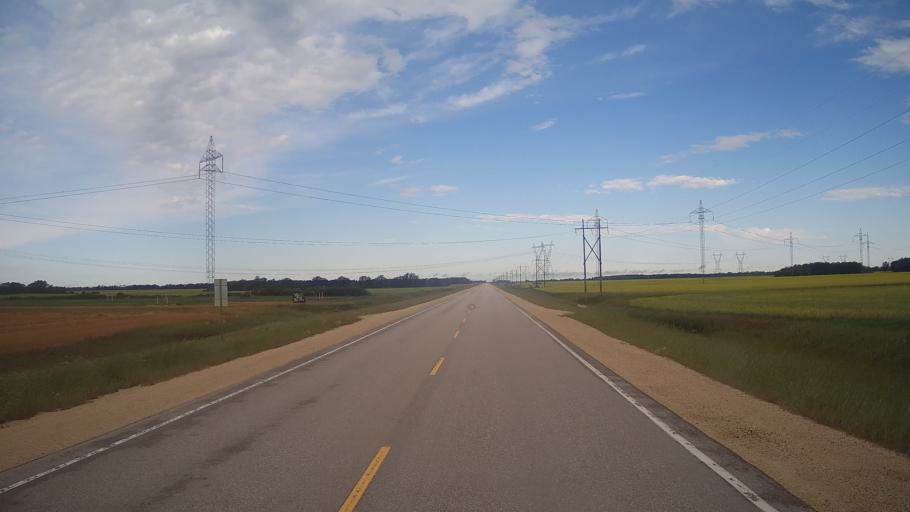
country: CA
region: Manitoba
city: Stonewall
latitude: 50.1228
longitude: -97.4833
